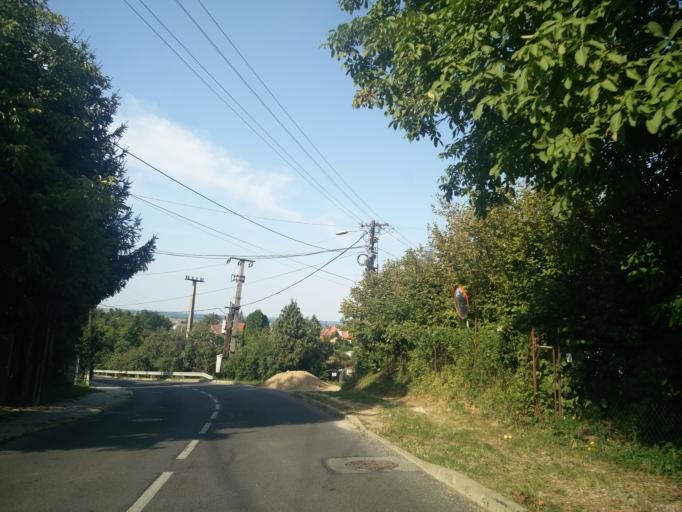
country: HU
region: Zala
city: Zalaegerszeg
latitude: 46.8242
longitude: 16.8216
